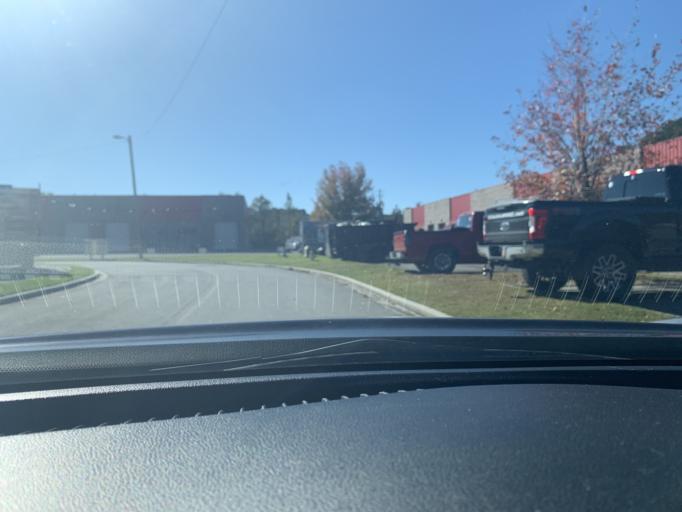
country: US
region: Georgia
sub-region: Chatham County
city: Pooler
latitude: 32.1241
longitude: -81.2636
